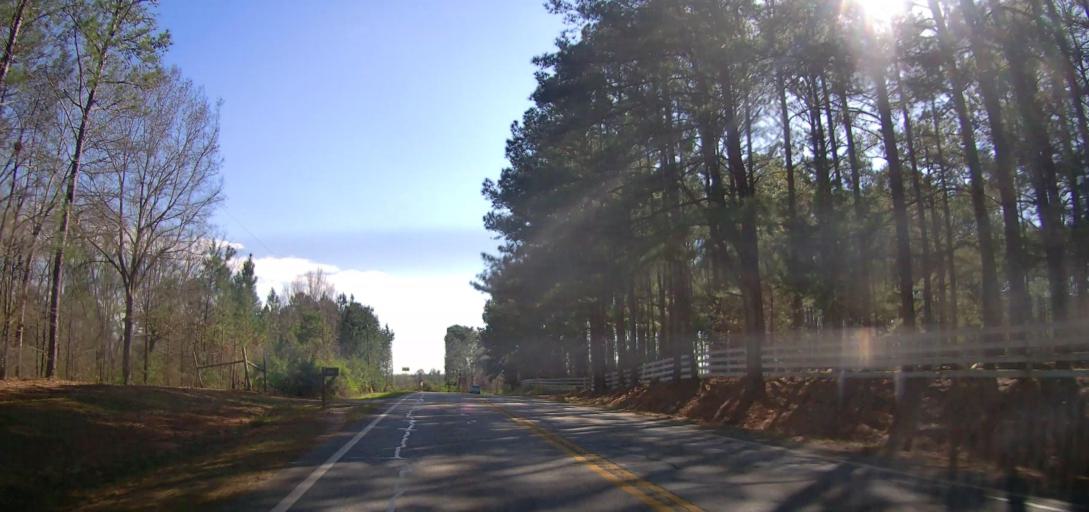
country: US
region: Georgia
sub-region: Butts County
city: Indian Springs
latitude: 33.2032
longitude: -83.9361
